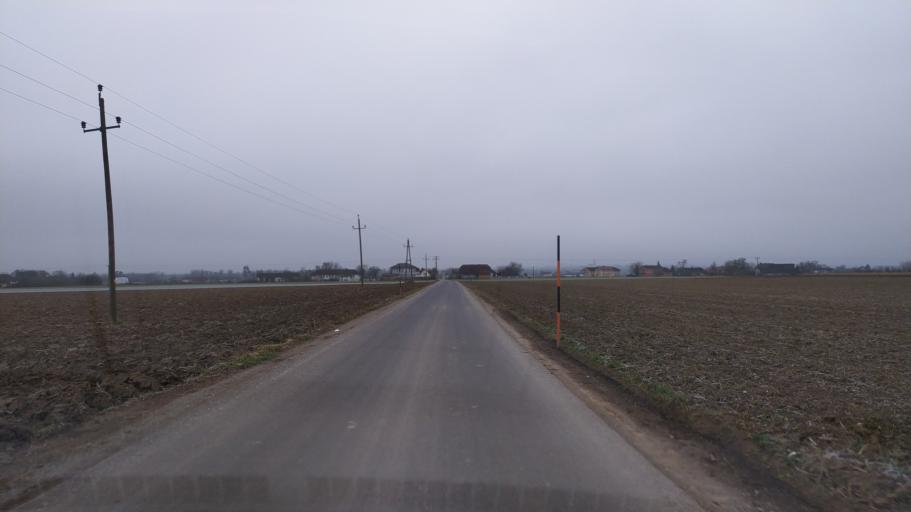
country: AT
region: Upper Austria
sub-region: Politischer Bezirk Perg
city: Perg
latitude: 48.2051
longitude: 14.7178
